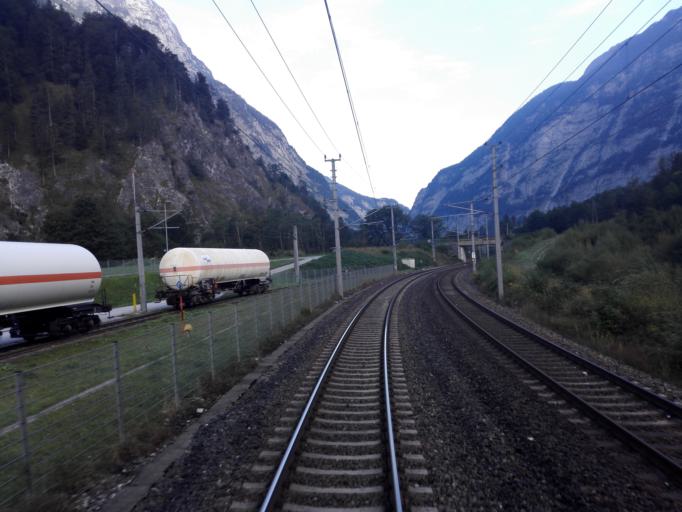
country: AT
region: Salzburg
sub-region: Politischer Bezirk Sankt Johann im Pongau
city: Werfen
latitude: 47.5249
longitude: 13.1660
